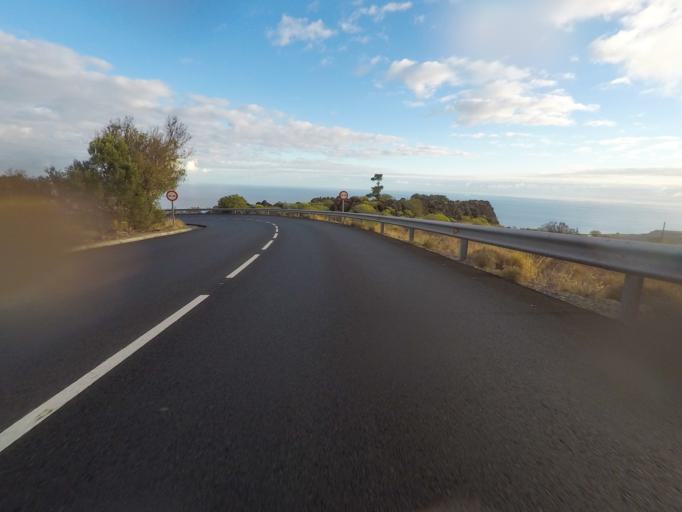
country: ES
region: Canary Islands
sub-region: Provincia de Santa Cruz de Tenerife
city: Alajero
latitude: 28.0490
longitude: -17.1984
